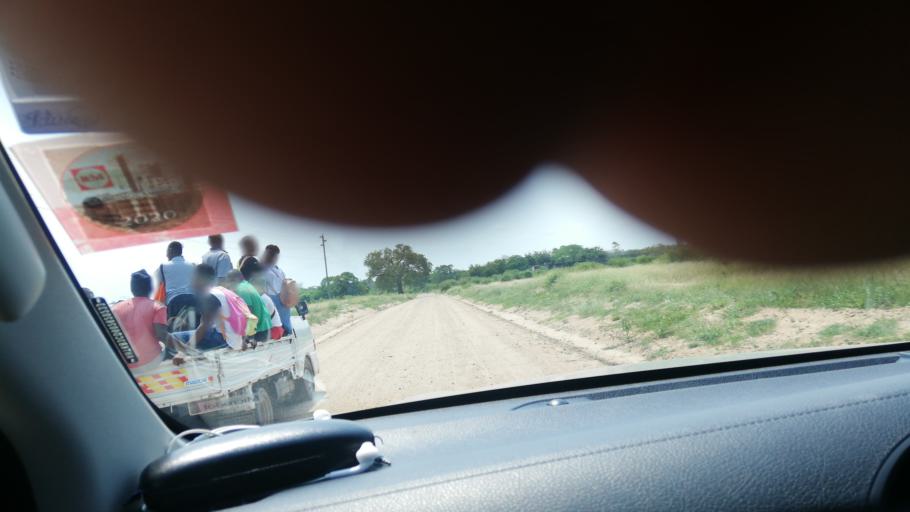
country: MZ
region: Maputo
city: Matola
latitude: -26.0621
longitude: 32.3901
